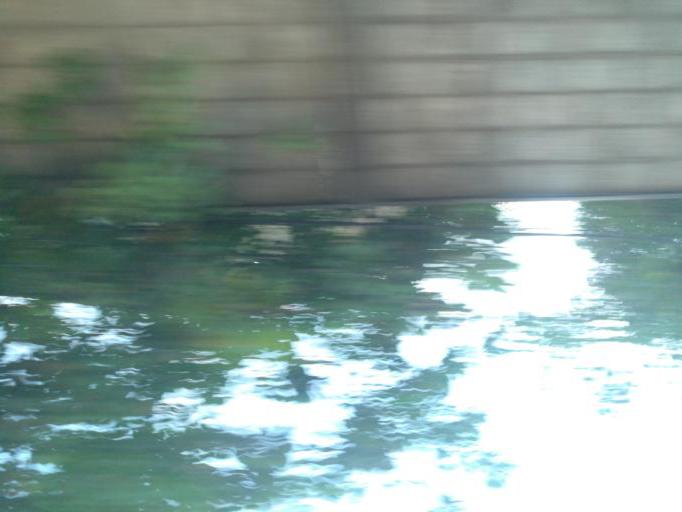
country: NG
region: Abuja Federal Capital Territory
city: Abuja
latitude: 9.0809
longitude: 7.3955
